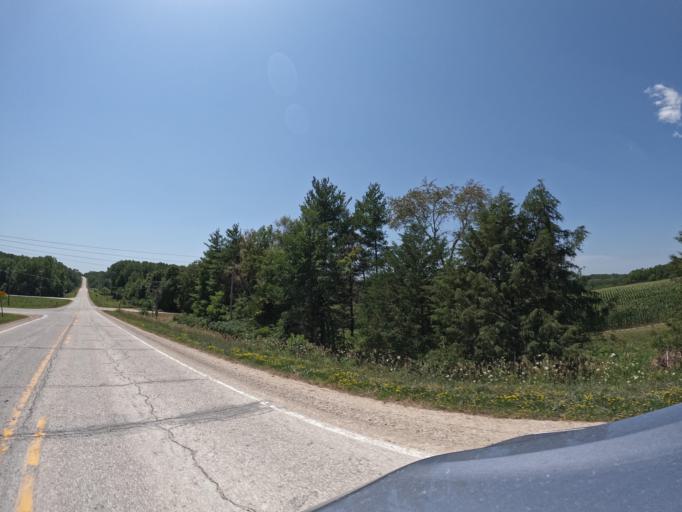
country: US
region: Iowa
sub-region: Henry County
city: Mount Pleasant
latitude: 40.9394
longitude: -91.6168
